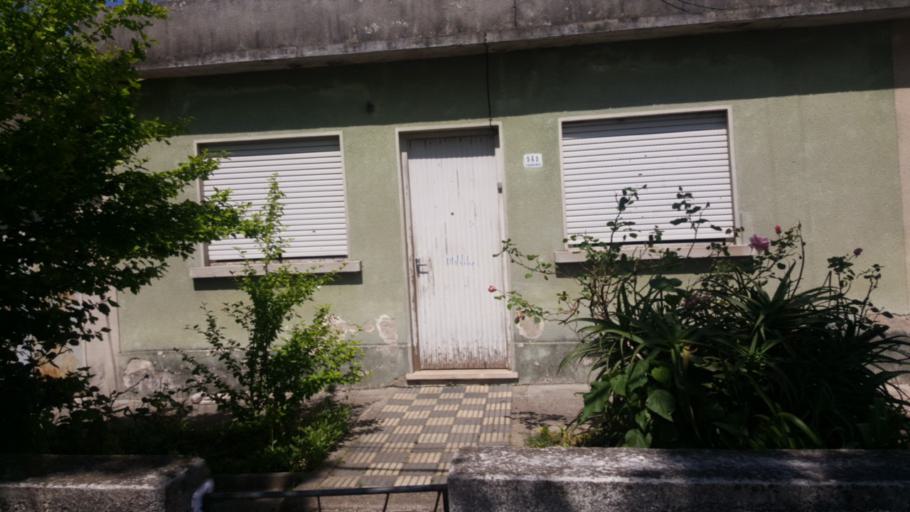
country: UY
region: Florida
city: Florida
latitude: -34.0971
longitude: -56.2216
